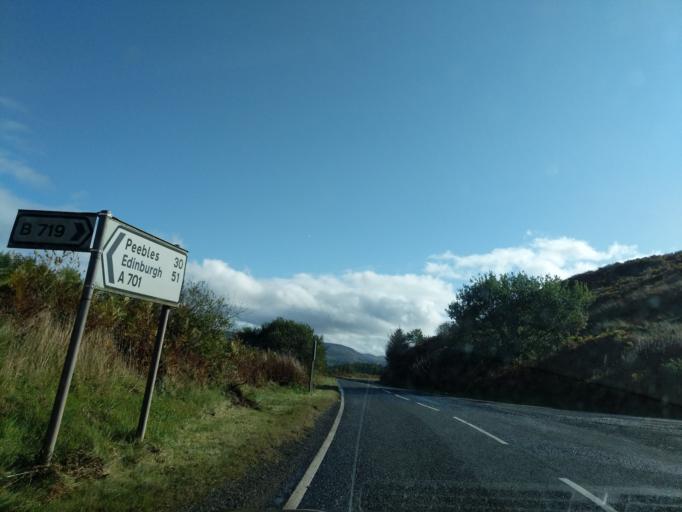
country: GB
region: Scotland
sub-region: Dumfries and Galloway
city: Moffat
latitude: 55.3613
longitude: -3.4768
